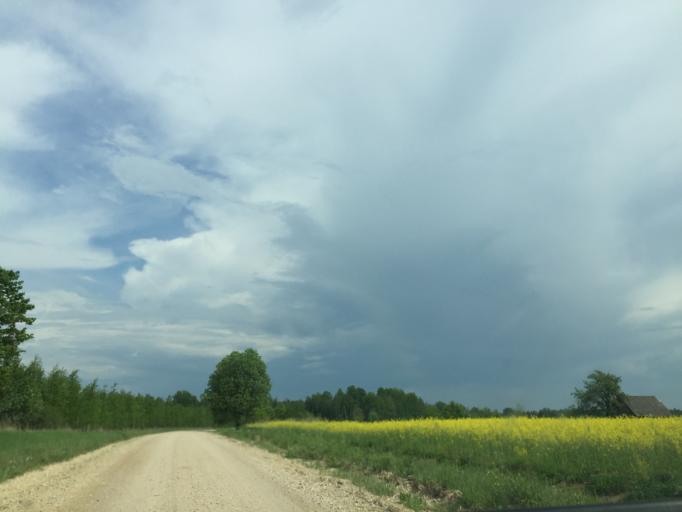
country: LV
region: Livani
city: Livani
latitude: 56.5870
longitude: 26.2033
